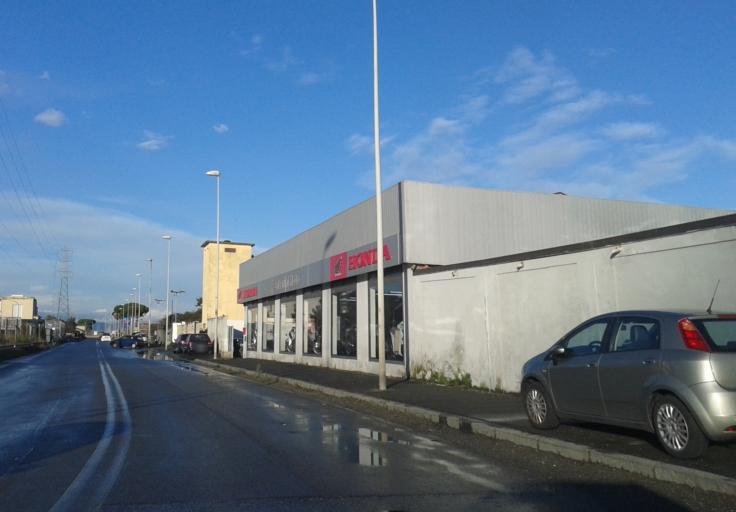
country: IT
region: Tuscany
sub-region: Provincia di Livorno
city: Livorno
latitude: 43.5719
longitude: 10.3188
